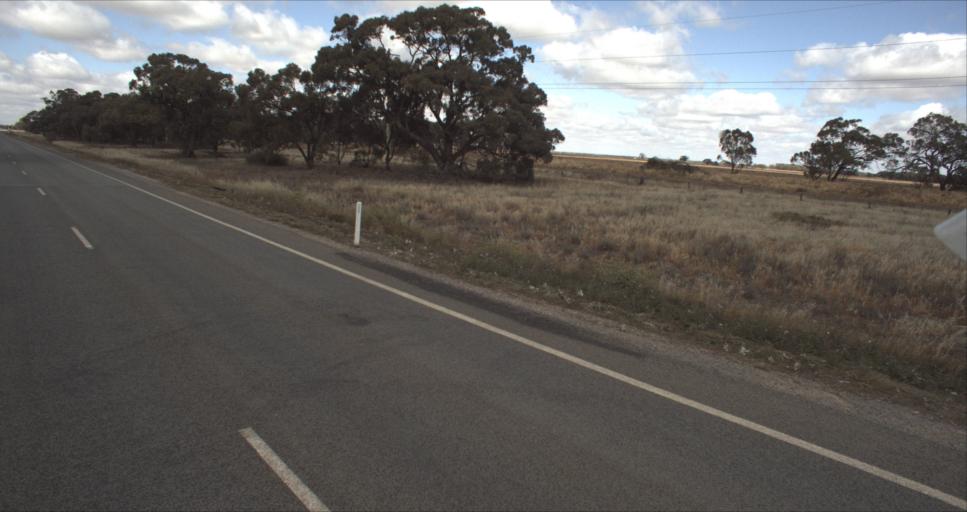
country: AU
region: New South Wales
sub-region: Murrumbidgee Shire
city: Darlington Point
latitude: -34.5705
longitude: 146.1673
